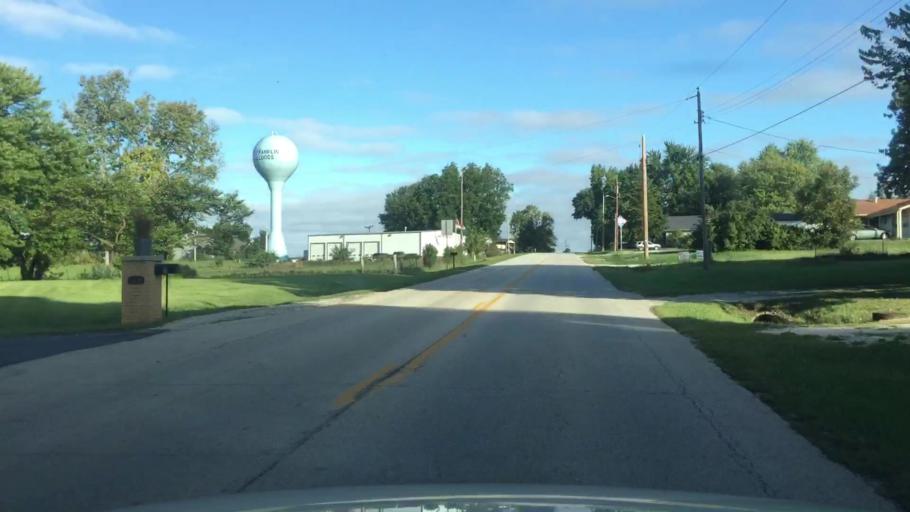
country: US
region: Missouri
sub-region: Howard County
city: New Franklin
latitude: 39.0222
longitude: -92.7460
